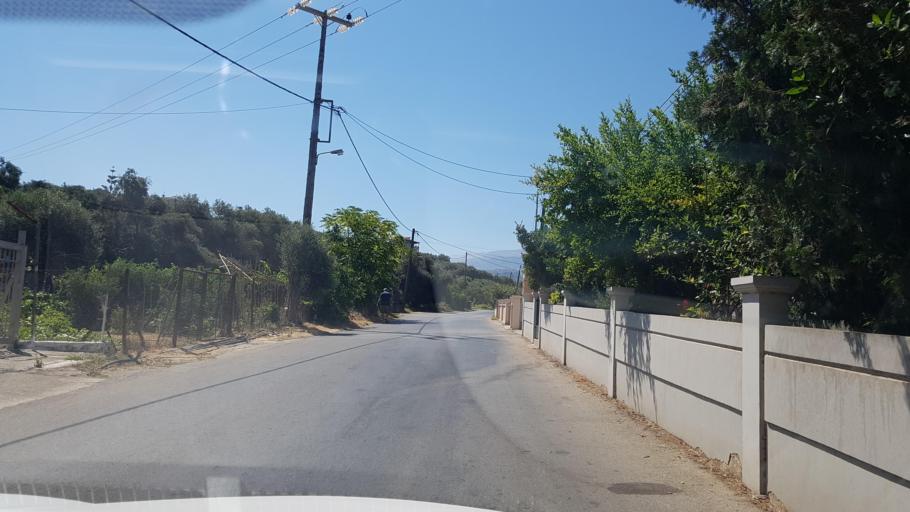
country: GR
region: Crete
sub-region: Nomos Chanias
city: Daratsos
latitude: 35.5044
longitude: 23.9893
